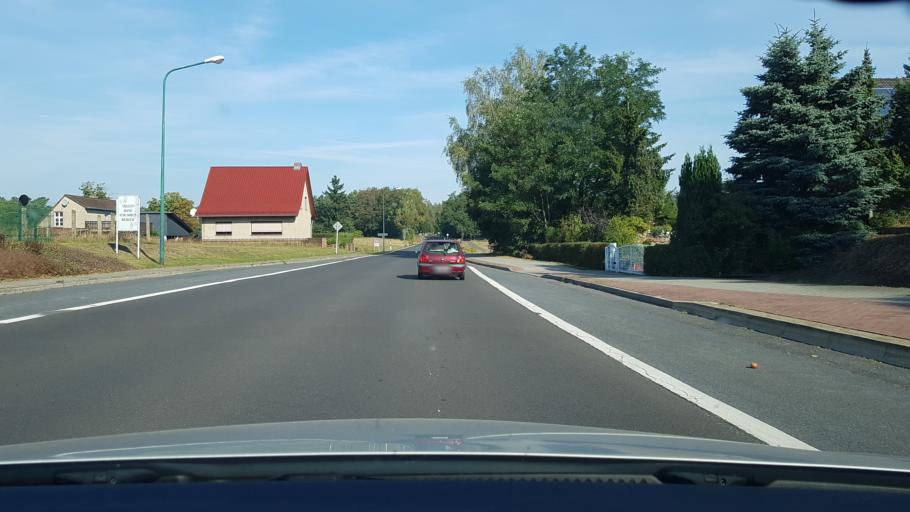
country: DE
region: Brandenburg
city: Mixdorf
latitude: 52.1426
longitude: 14.4165
